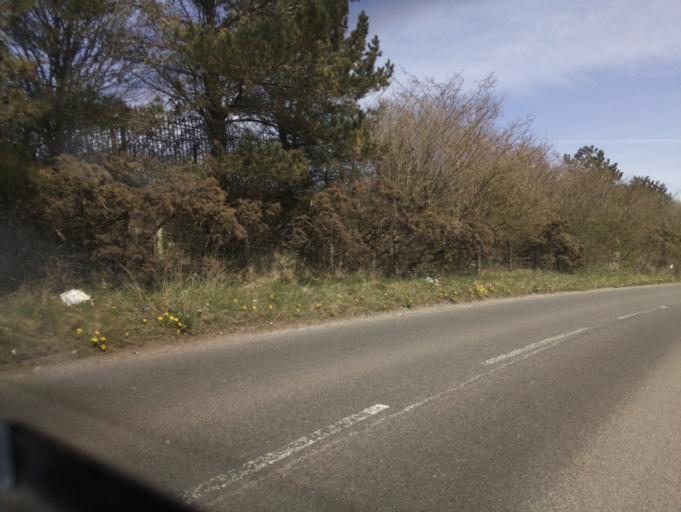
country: GB
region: Wales
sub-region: Caerphilly County Borough
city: Rhymney
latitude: 51.7685
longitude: -3.3312
